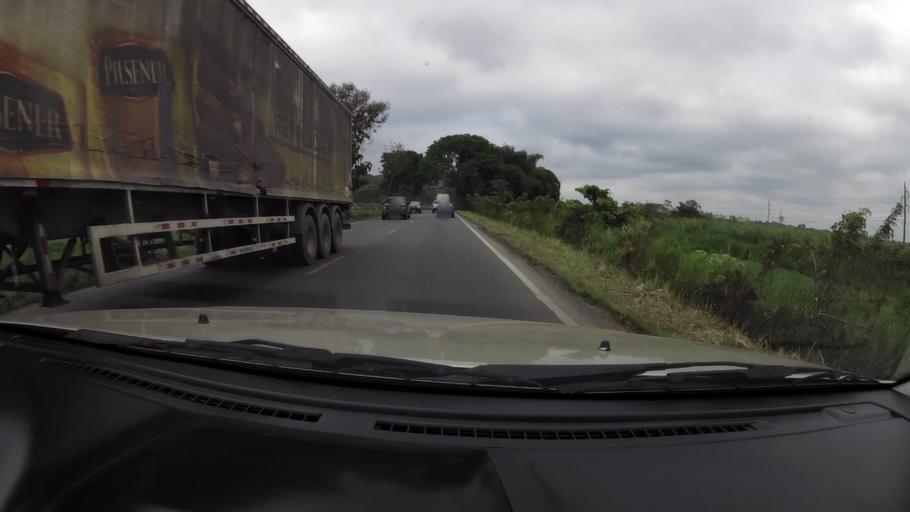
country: EC
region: Guayas
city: Naranjal
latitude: -2.7733
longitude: -79.6955
